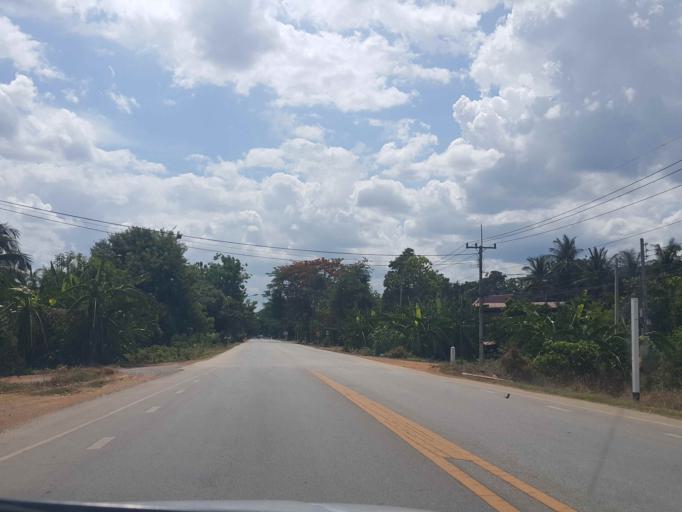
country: TH
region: Sukhothai
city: Thung Saliam
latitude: 17.3283
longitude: 99.6274
